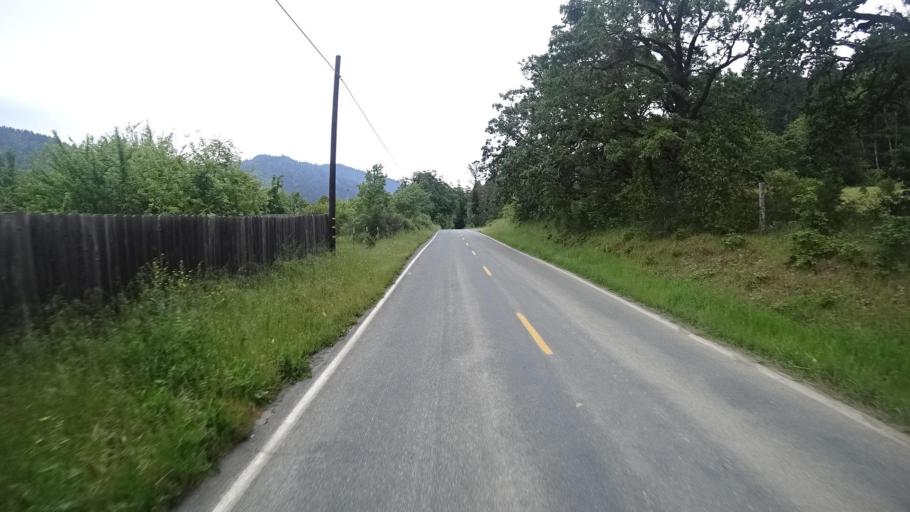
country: US
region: California
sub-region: Humboldt County
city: Willow Creek
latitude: 41.0790
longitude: -123.6992
